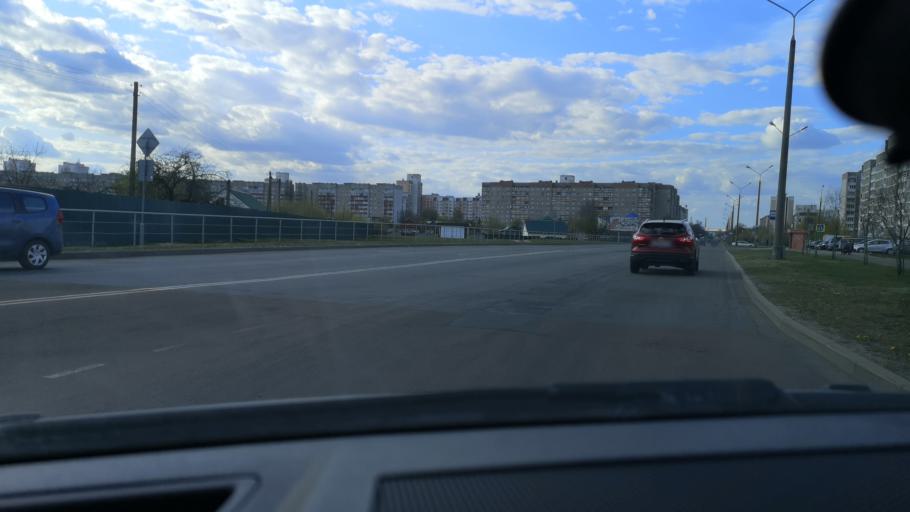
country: BY
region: Gomel
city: Gomel
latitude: 52.3993
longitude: 30.9228
